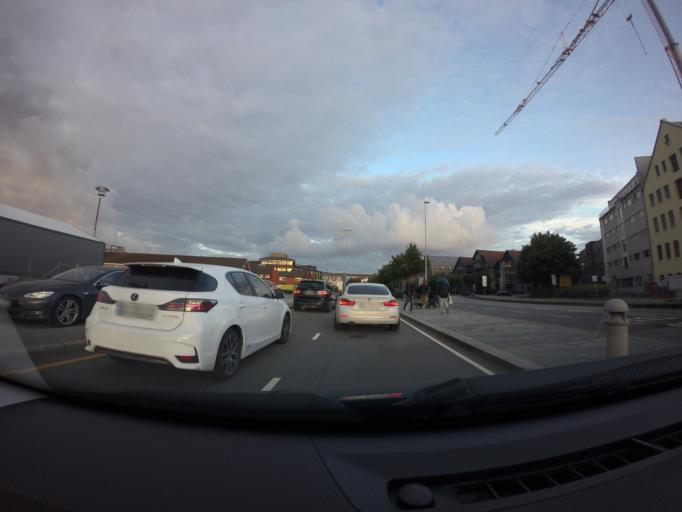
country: NO
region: Rogaland
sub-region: Stavanger
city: Stavanger
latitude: 58.9715
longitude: 5.7421
